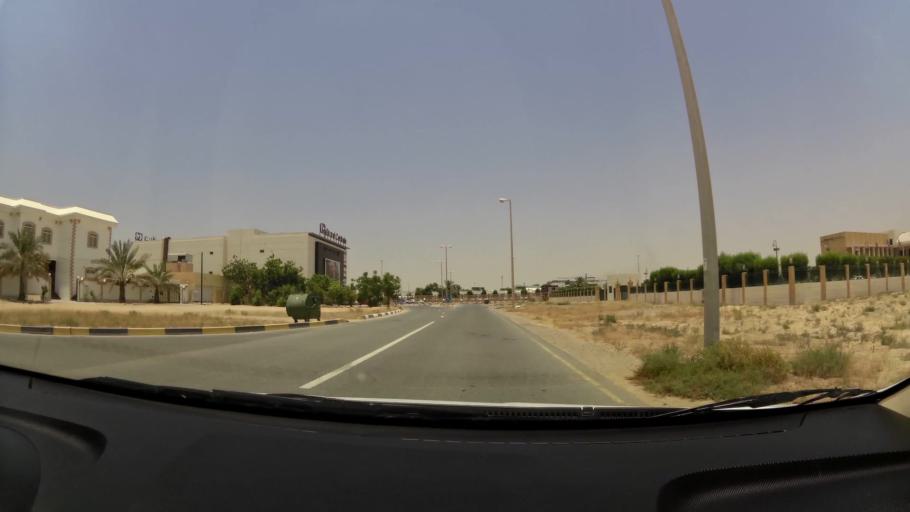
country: AE
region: Ajman
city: Ajman
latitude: 25.4137
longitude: 55.4958
